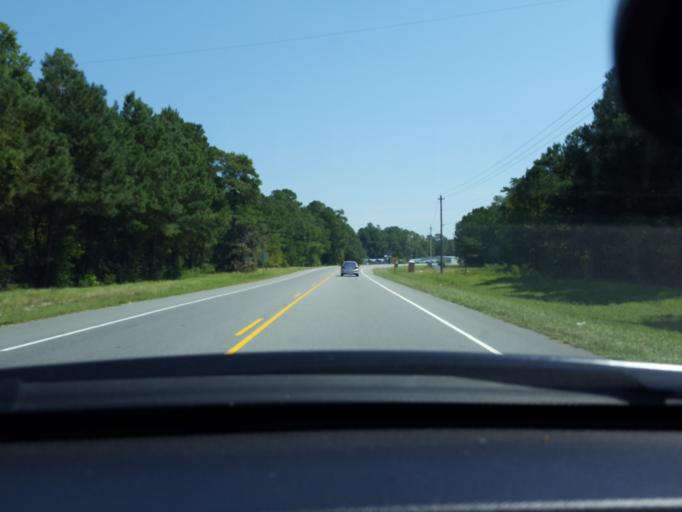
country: US
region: North Carolina
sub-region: Bladen County
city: Elizabethtown
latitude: 34.6564
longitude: -78.5103
